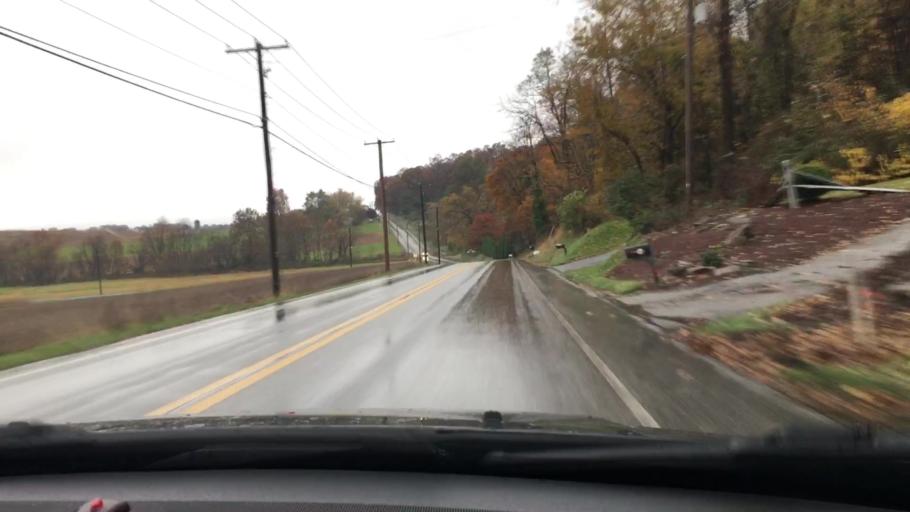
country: US
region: Pennsylvania
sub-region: Lancaster County
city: Quarryville
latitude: 39.8630
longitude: -76.2625
